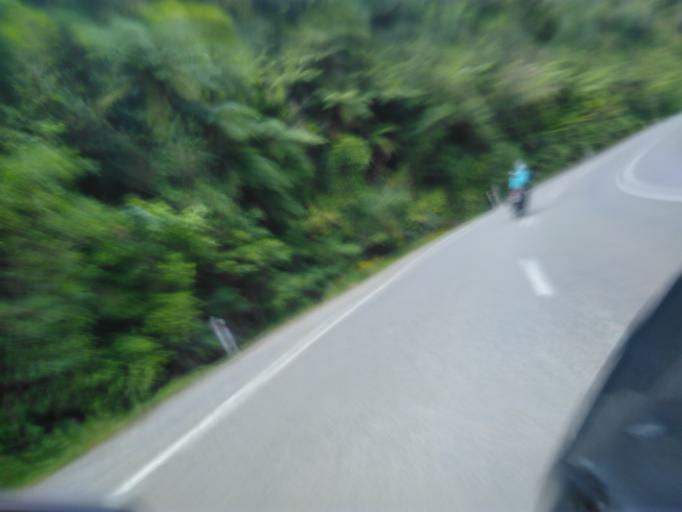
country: NZ
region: Bay of Plenty
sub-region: Opotiki District
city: Opotiki
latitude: -38.2876
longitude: 177.3619
